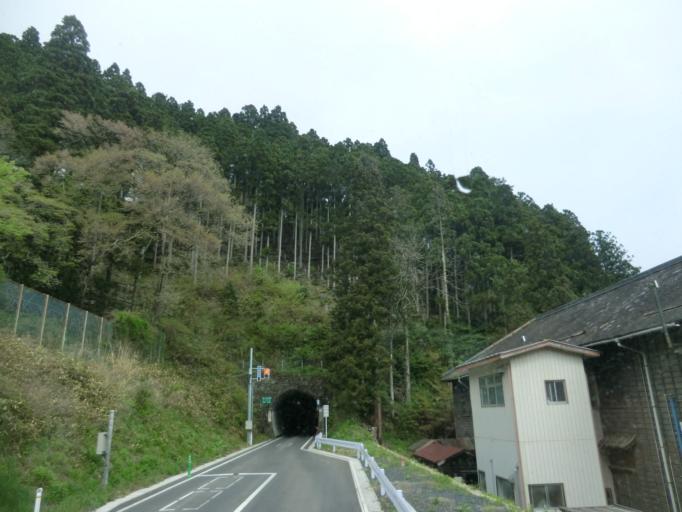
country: JP
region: Iwate
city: Ofunato
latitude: 38.9101
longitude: 141.5739
